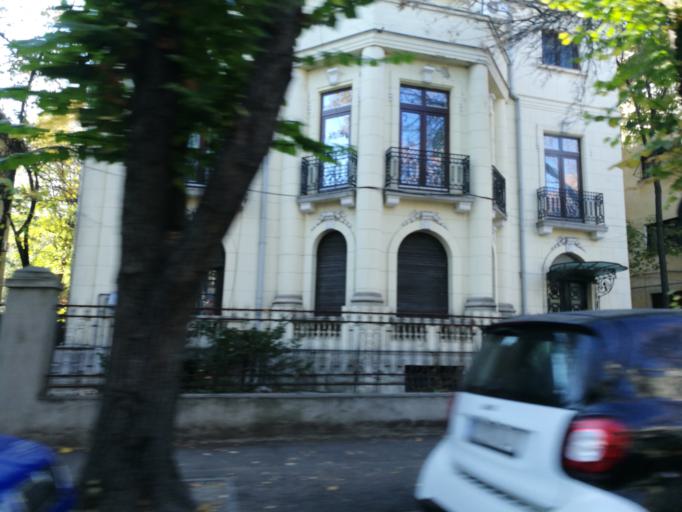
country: RO
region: Bucuresti
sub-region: Municipiul Bucuresti
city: Bucharest
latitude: 44.4563
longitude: 26.0941
